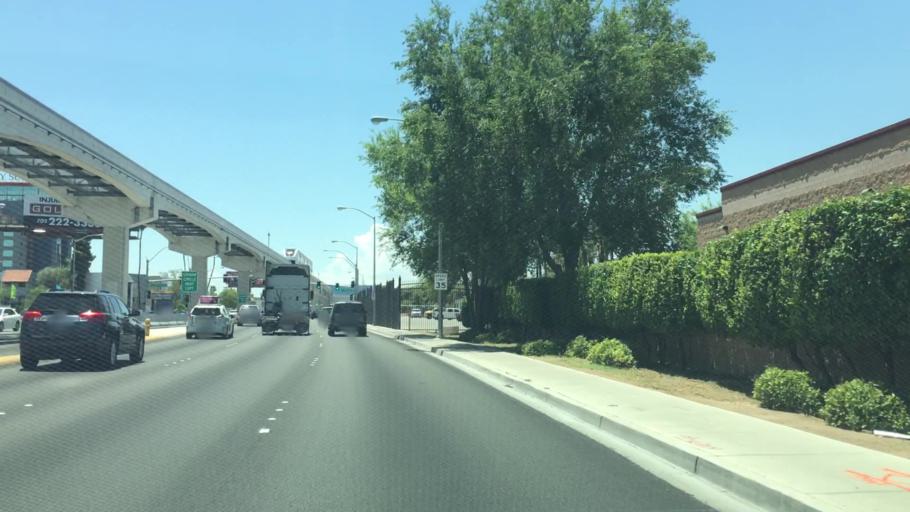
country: US
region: Nevada
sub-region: Clark County
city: Paradise
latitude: 36.1263
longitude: -115.1551
